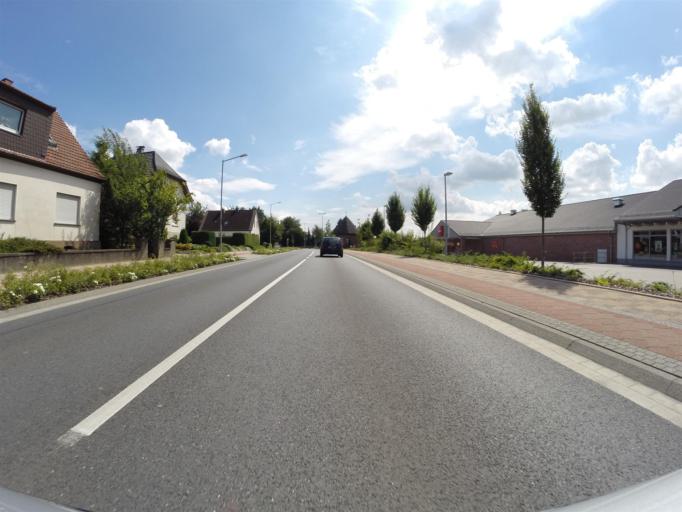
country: DE
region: North Rhine-Westphalia
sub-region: Regierungsbezirk Detmold
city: Hiddenhausen
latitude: 52.1502
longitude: 8.6481
